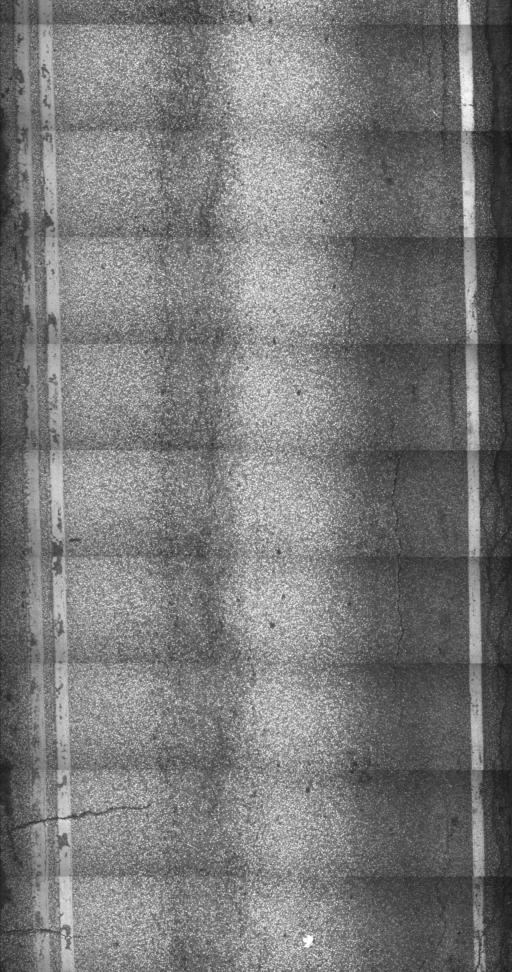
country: US
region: Vermont
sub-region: Washington County
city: Northfield
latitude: 44.1061
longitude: -72.6446
